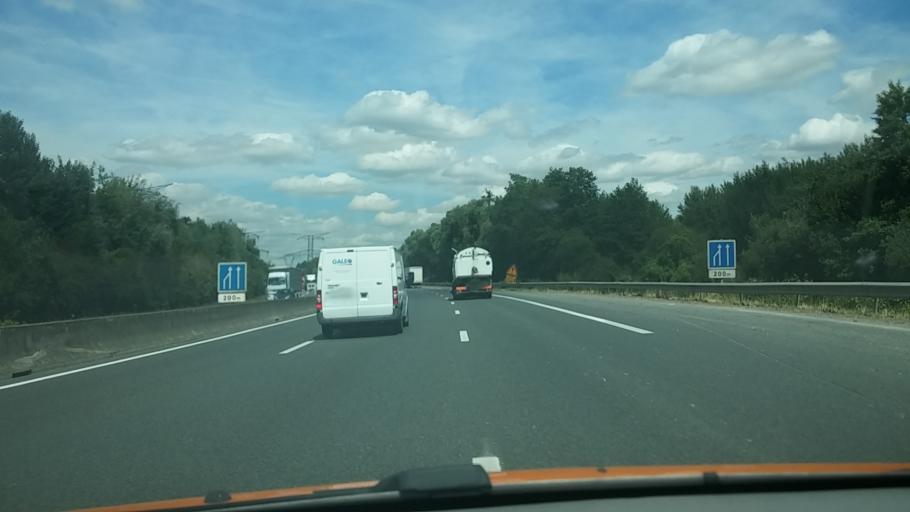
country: FR
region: Ile-de-France
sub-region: Departement de Seine-et-Marne
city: Pomponne
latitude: 48.8901
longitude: 2.6676
